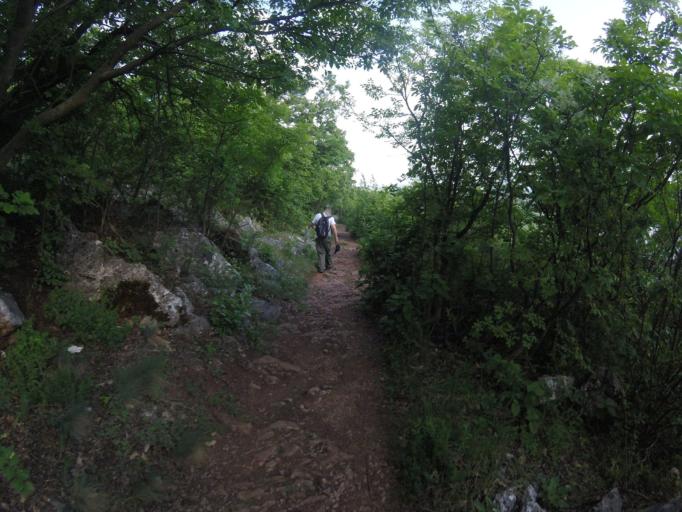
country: SK
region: Kosicky
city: Medzev
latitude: 48.6125
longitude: 20.8701
